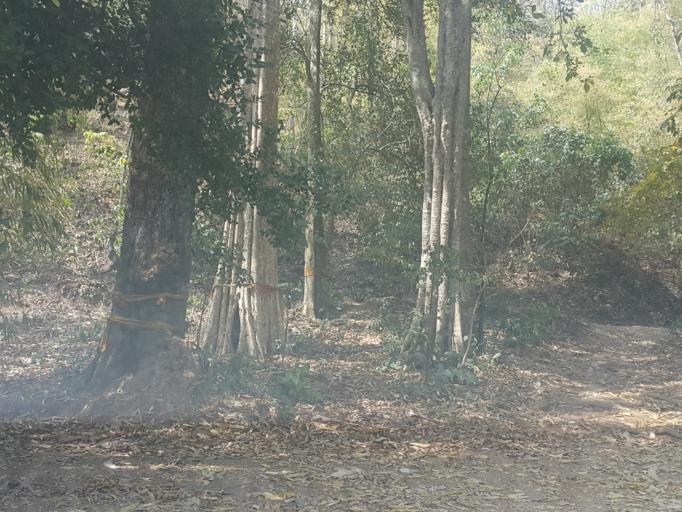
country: TH
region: Chiang Mai
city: Hang Dong
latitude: 18.7507
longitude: 98.8269
